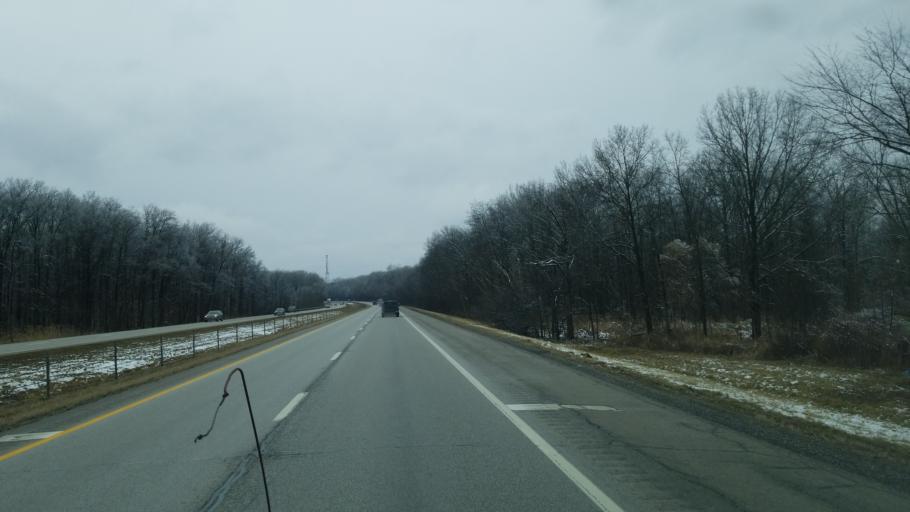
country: US
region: Ohio
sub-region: Portage County
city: Ravenna
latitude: 41.1111
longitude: -81.2714
